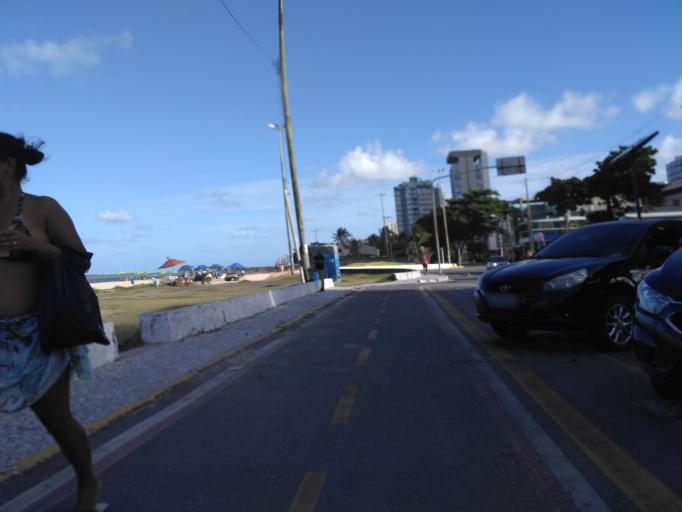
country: BR
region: Pernambuco
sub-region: Jaboatao Dos Guararapes
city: Jaboatao
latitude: -8.1672
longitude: -34.9138
